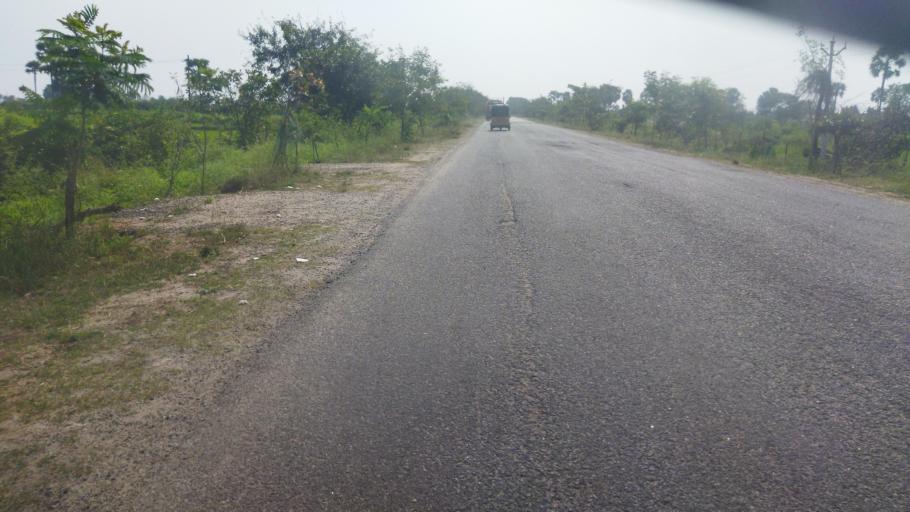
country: IN
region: Telangana
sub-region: Nalgonda
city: Nalgonda
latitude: 17.1062
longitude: 79.2806
